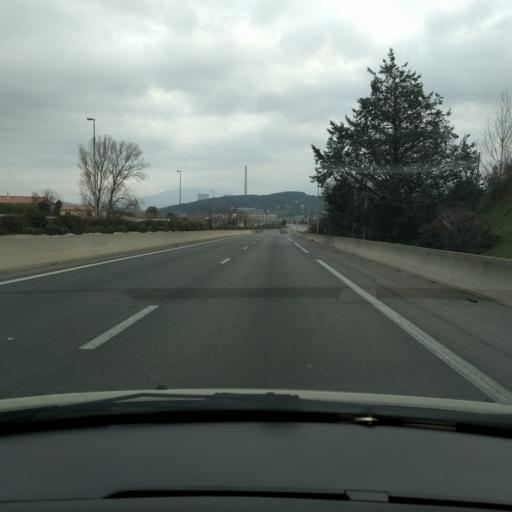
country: FR
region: Provence-Alpes-Cote d'Azur
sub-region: Departement des Bouches-du-Rhone
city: Gardanne
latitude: 43.4545
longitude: 5.4563
